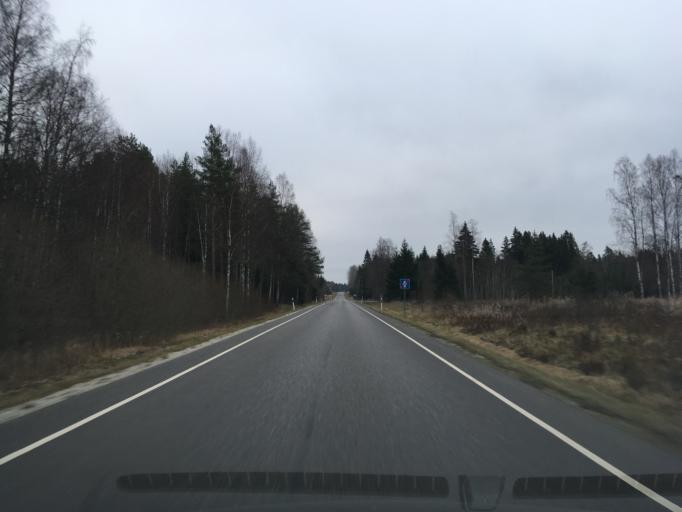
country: EE
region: Laeaene-Virumaa
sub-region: Tapa vald
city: Tapa
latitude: 59.4571
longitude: 25.9749
